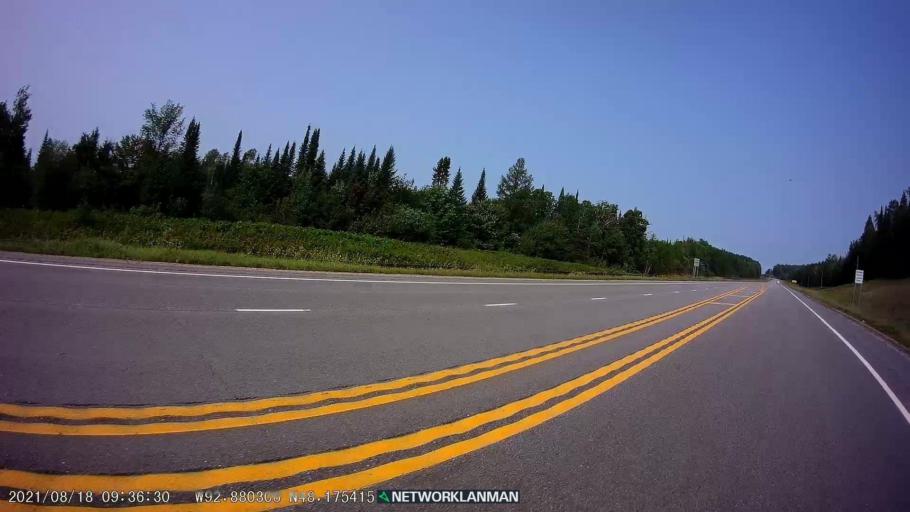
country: CA
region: Ontario
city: Fort Frances
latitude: 48.1756
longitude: -92.8804
